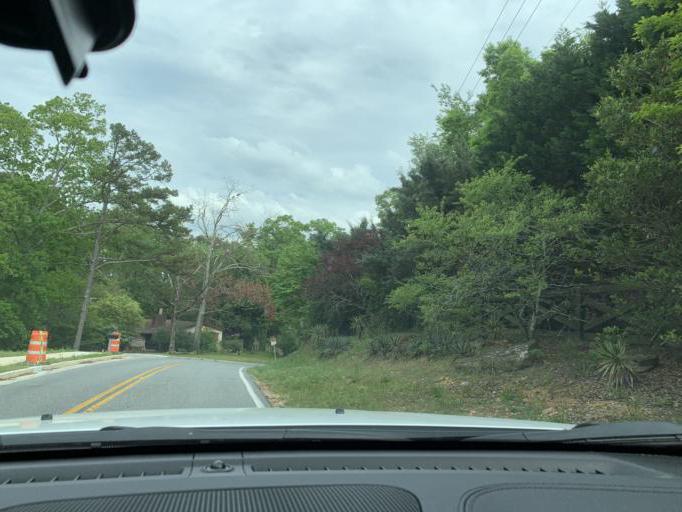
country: US
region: Georgia
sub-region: Gwinnett County
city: Suwanee
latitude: 34.1168
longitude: -84.1143
